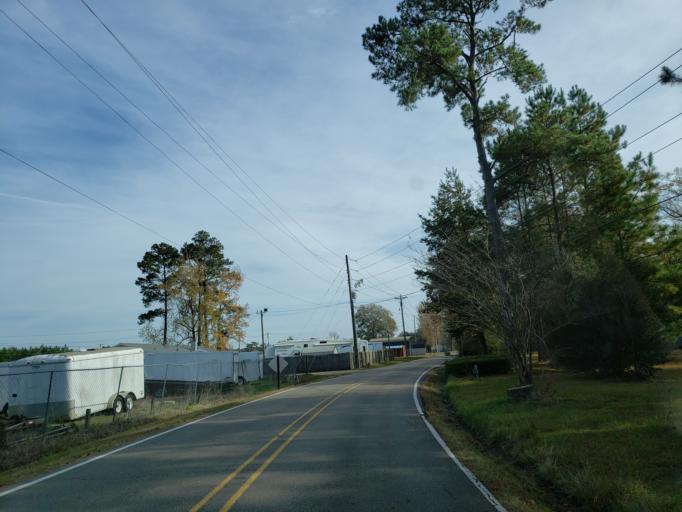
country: US
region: Mississippi
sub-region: Forrest County
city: Rawls Springs
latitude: 31.3865
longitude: -89.3749
